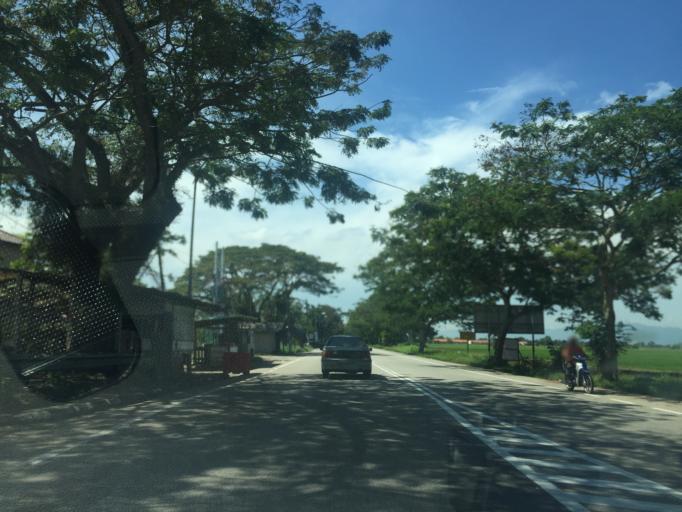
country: MY
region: Penang
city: Tasek Glugor
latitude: 5.4609
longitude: 100.4488
